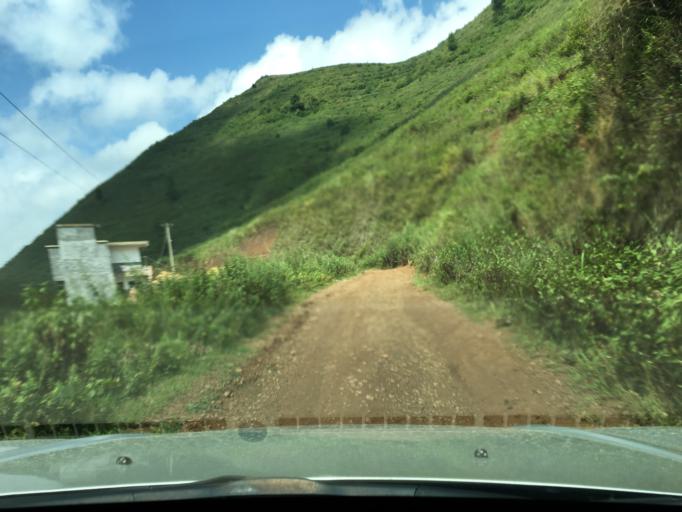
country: CN
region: Guizhou Sheng
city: Liupanshui
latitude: 25.9079
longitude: 105.1172
